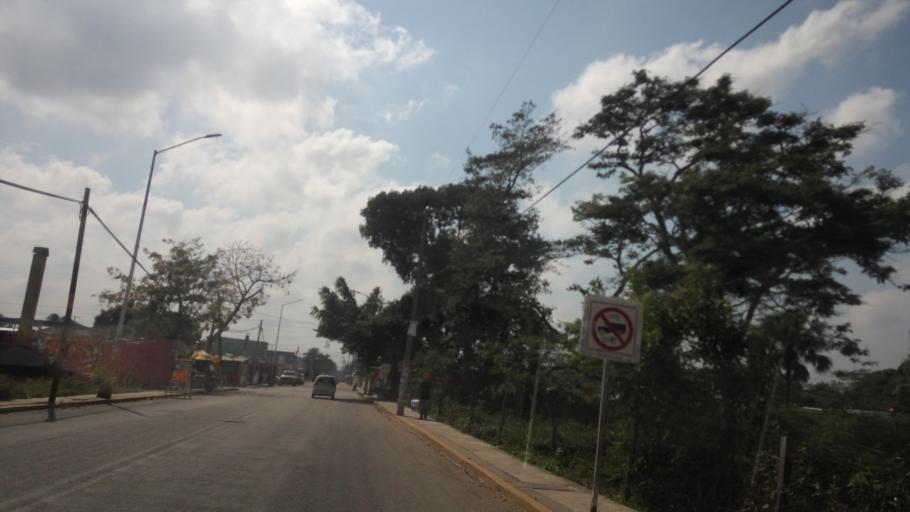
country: MX
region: Tabasco
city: Frontera
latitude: 18.5295
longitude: -92.6377
